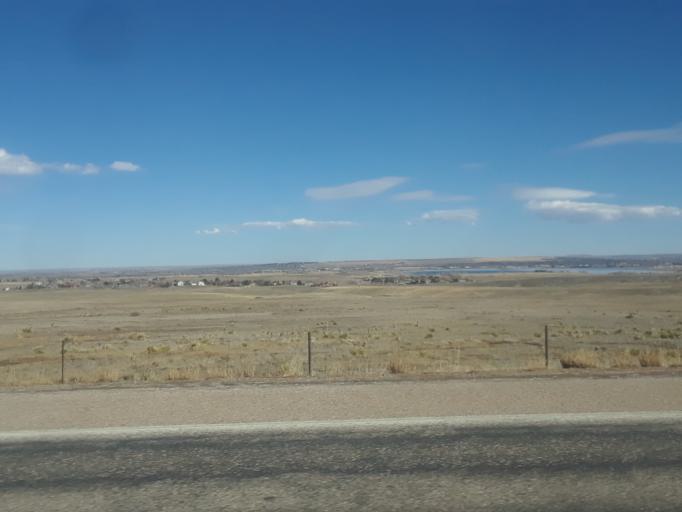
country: US
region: Colorado
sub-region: Boulder County
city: Boulder
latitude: 40.0908
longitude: -105.2822
